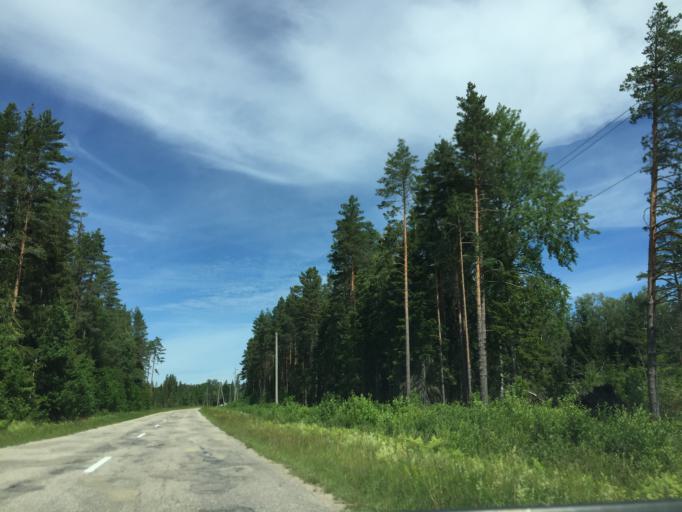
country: LV
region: Dundaga
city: Dundaga
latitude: 57.5655
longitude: 22.3096
